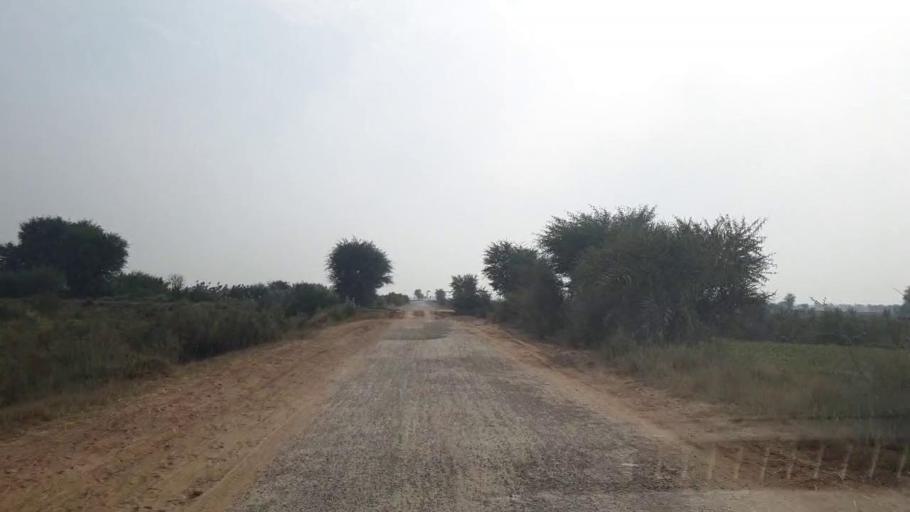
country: PK
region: Sindh
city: Sann
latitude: 26.0096
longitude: 68.1458
